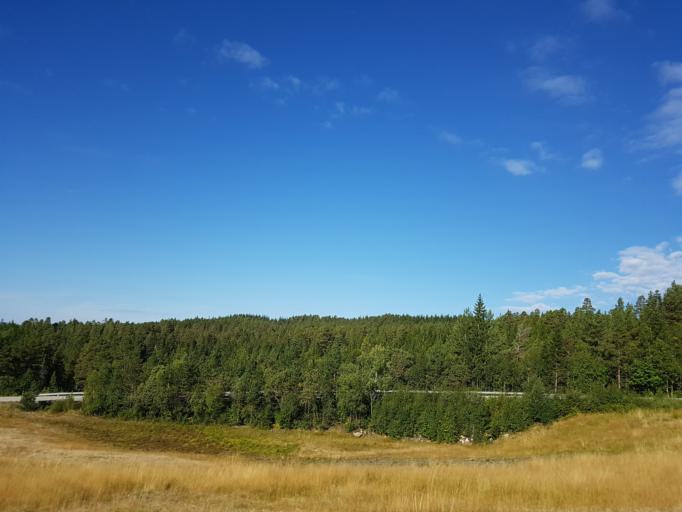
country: NO
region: Sor-Trondelag
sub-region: Trondheim
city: Trondheim
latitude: 63.6348
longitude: 10.2676
